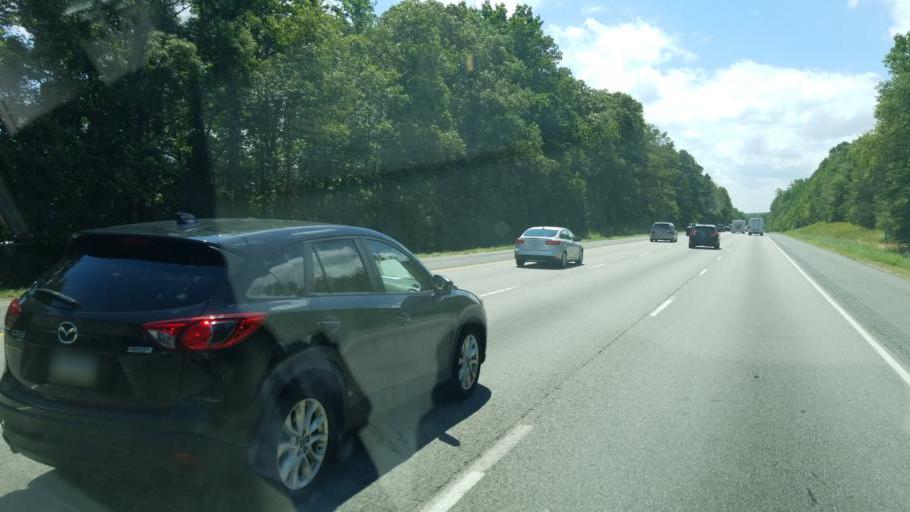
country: US
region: Virginia
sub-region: Hanover County
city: Ashland
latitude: 37.9120
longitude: -77.4592
